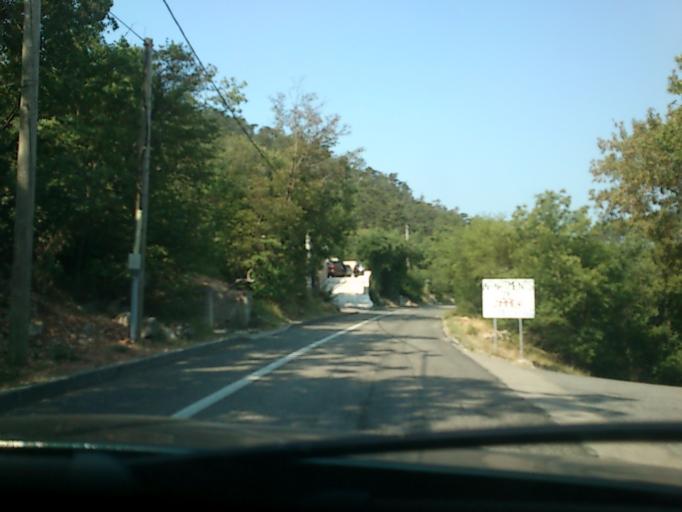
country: HR
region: Primorsko-Goranska
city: Banjol
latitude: 44.7040
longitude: 14.9000
